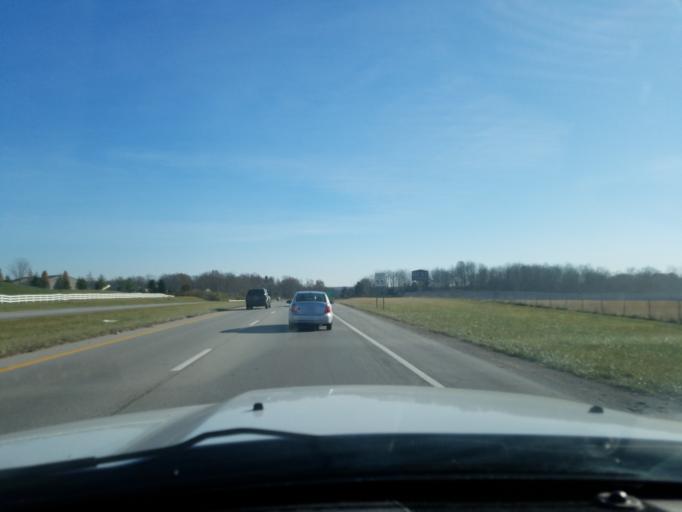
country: US
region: Ohio
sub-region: Clermont County
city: Batavia
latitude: 39.0883
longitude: -84.2130
